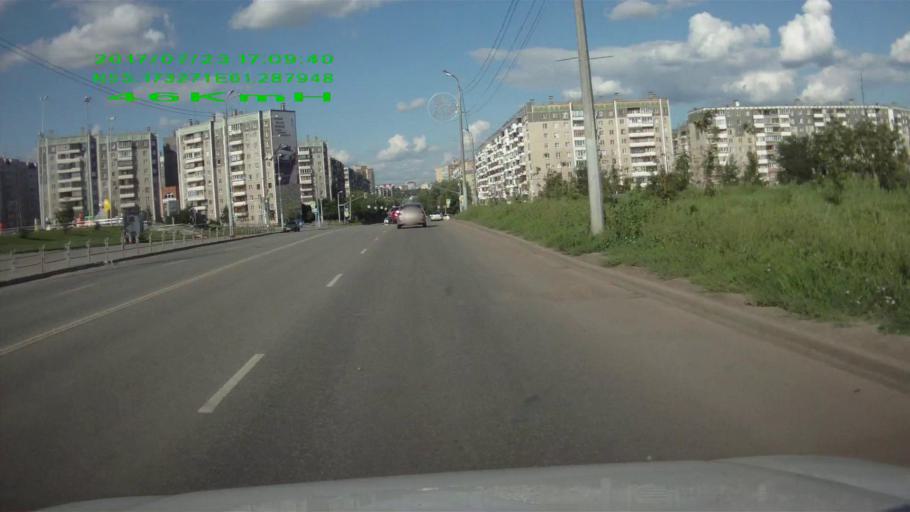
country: RU
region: Chelyabinsk
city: Roshchino
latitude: 55.1735
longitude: 61.2886
